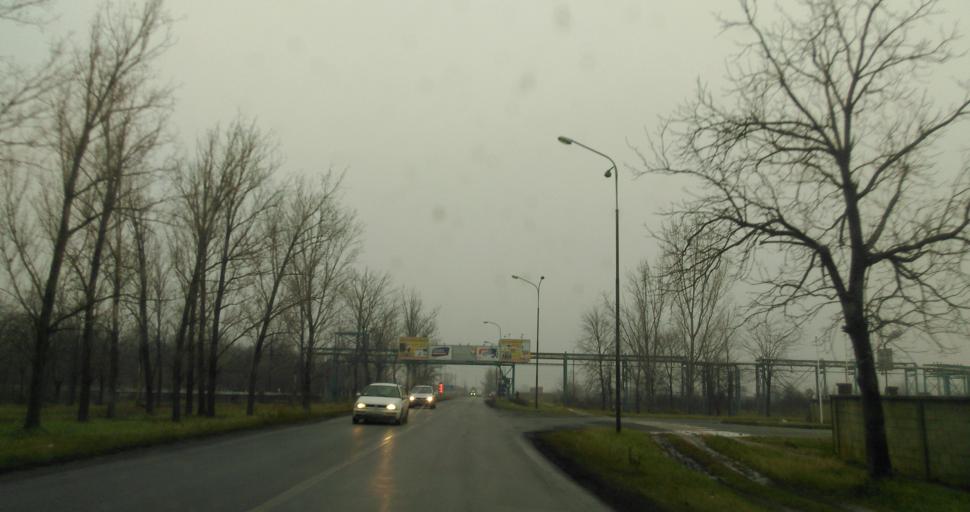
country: RS
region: Autonomna Pokrajina Vojvodina
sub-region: Srednjebanatski Okrug
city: Zrenjanin
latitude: 45.3669
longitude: 20.4225
